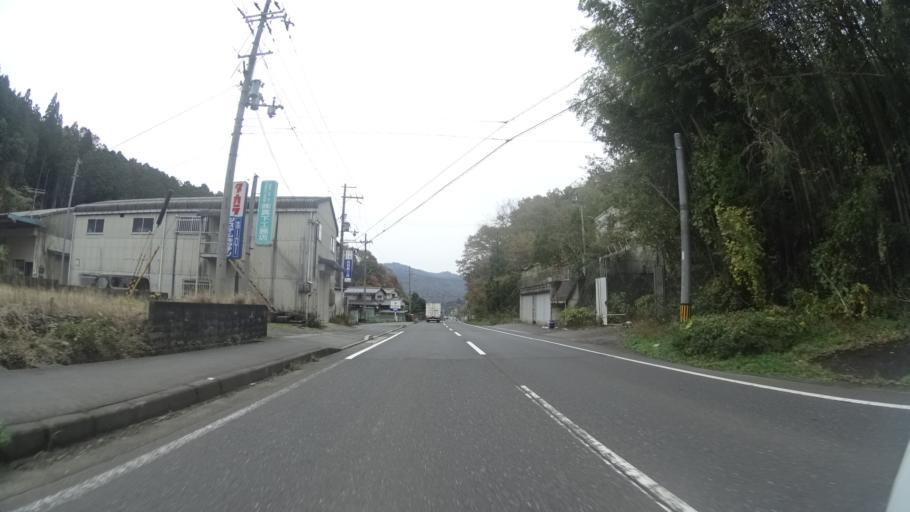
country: JP
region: Kyoto
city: Maizuru
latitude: 35.4685
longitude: 135.4237
